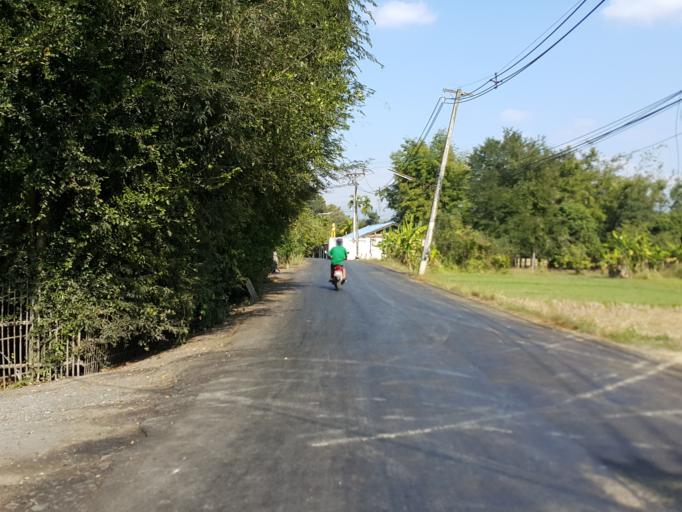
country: TH
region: Chiang Mai
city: Mae On
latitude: 18.8315
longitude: 99.2074
